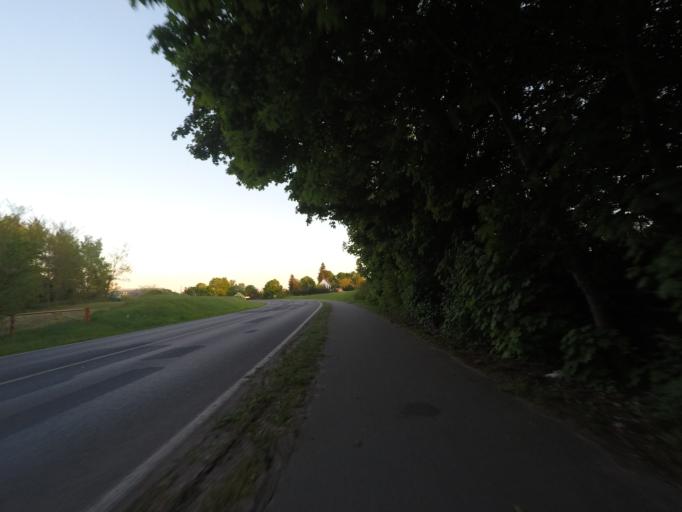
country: DE
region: Brandenburg
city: Melchow
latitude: 52.8453
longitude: 13.6901
